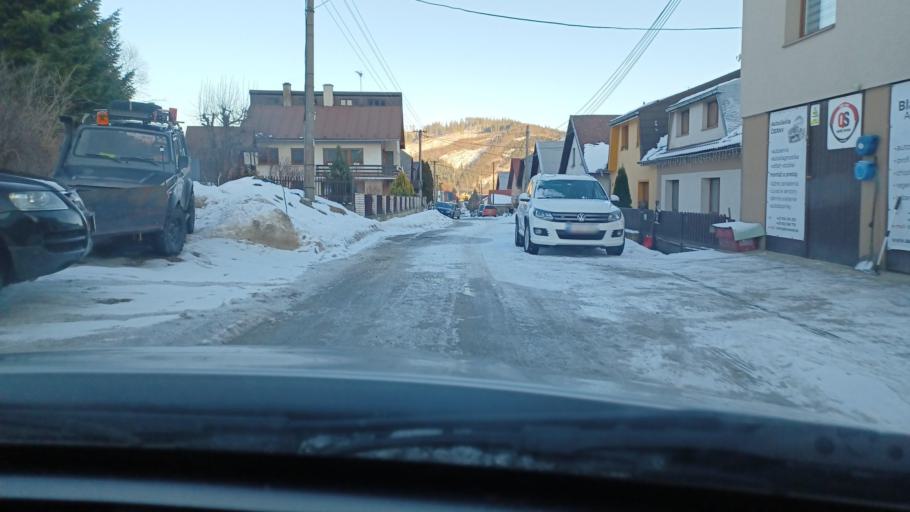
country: SK
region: Zilinsky
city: Tvrdosin
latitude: 49.3625
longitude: 19.5412
